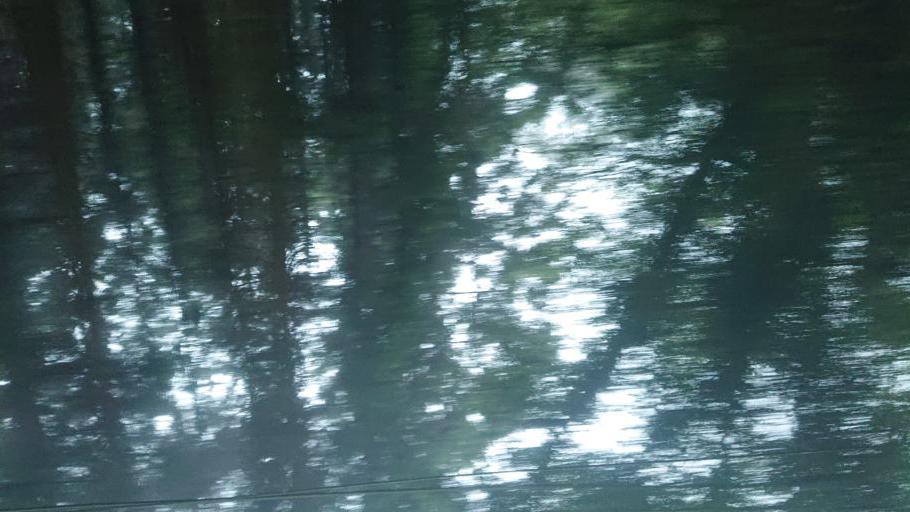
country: TW
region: Taiwan
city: Lugu
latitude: 23.5096
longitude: 120.7019
